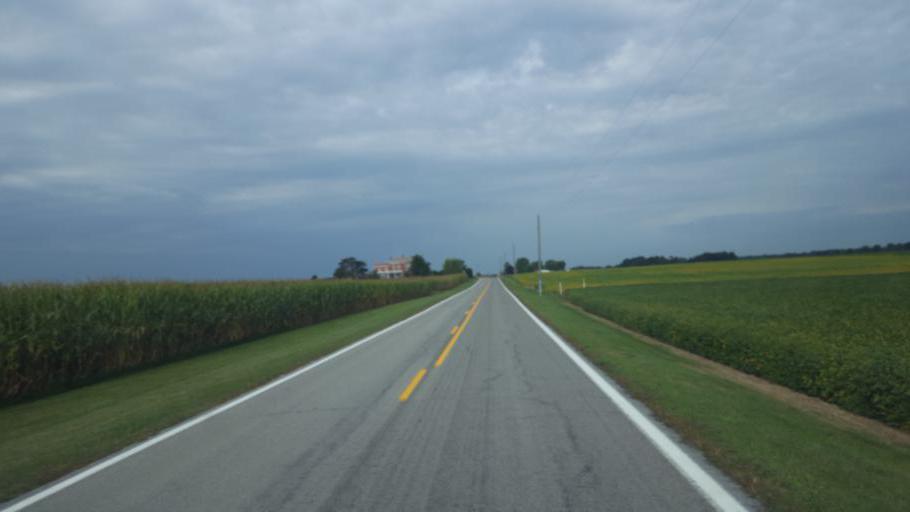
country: US
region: Ohio
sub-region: Wyandot County
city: Upper Sandusky
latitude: 40.7400
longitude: -83.1792
